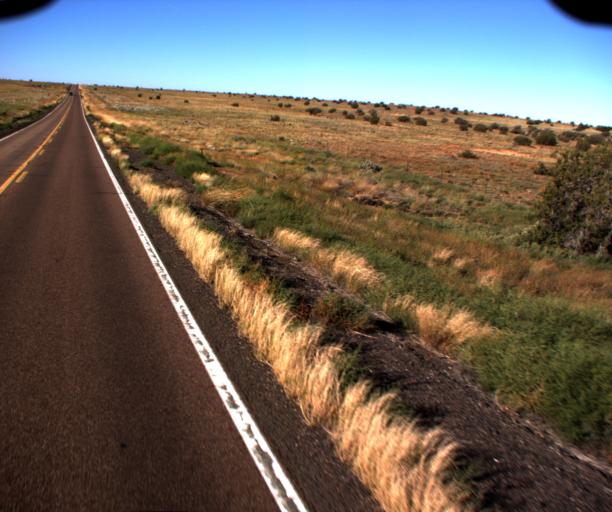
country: US
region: Arizona
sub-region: Navajo County
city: Holbrook
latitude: 34.7513
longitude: -110.2578
